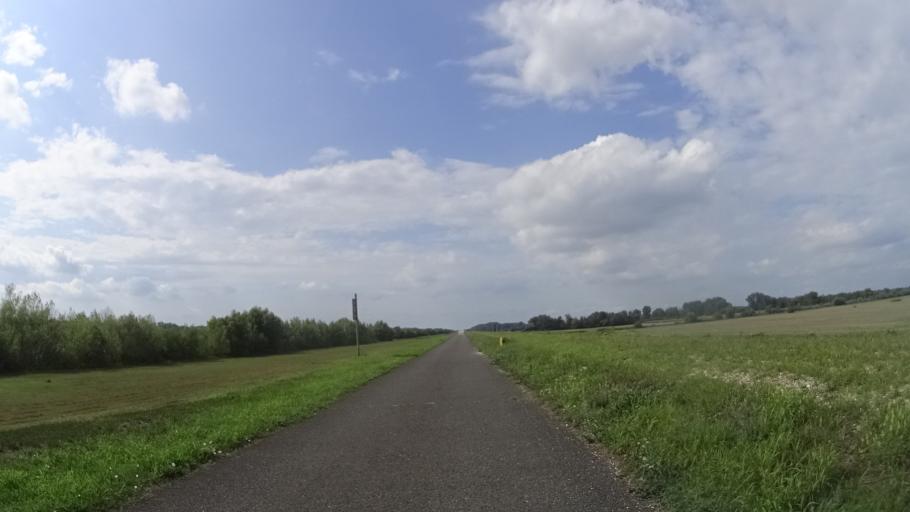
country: SK
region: Trnavsky
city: Gabcikovo
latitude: 47.8302
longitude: 17.6015
